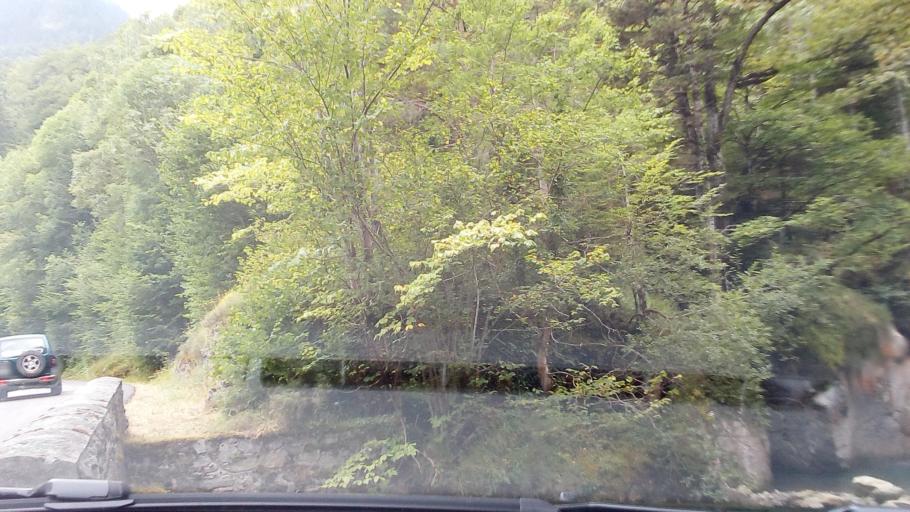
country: FR
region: Aquitaine
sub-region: Departement des Pyrenees-Atlantiques
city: Laruns
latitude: 42.9311
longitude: -0.4482
